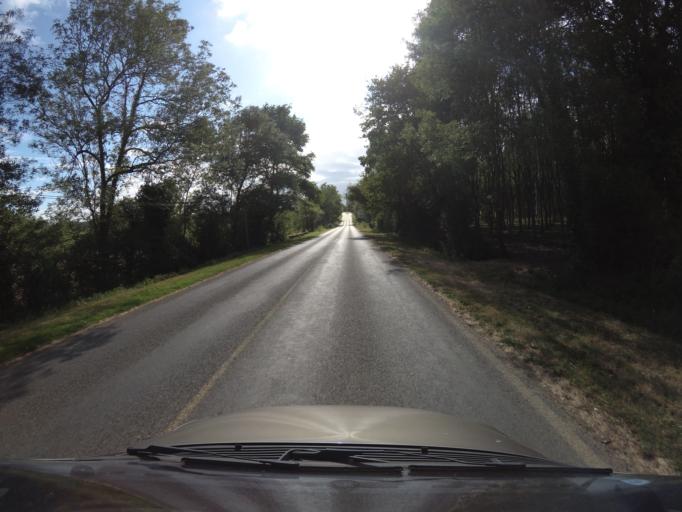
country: FR
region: Pays de la Loire
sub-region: Departement de Maine-et-Loire
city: Coron
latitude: 47.1259
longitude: -0.6576
